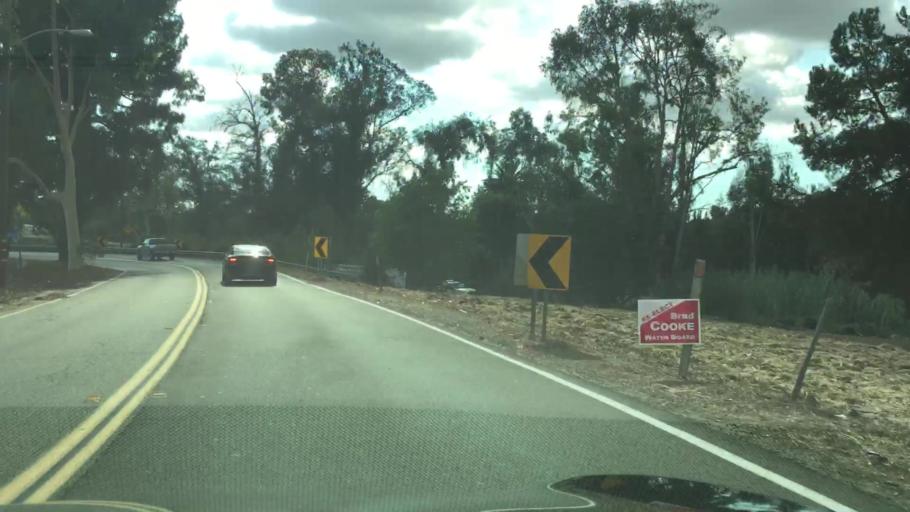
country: US
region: California
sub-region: Los Angeles County
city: La Habra Heights
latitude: 33.9490
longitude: -117.9642
